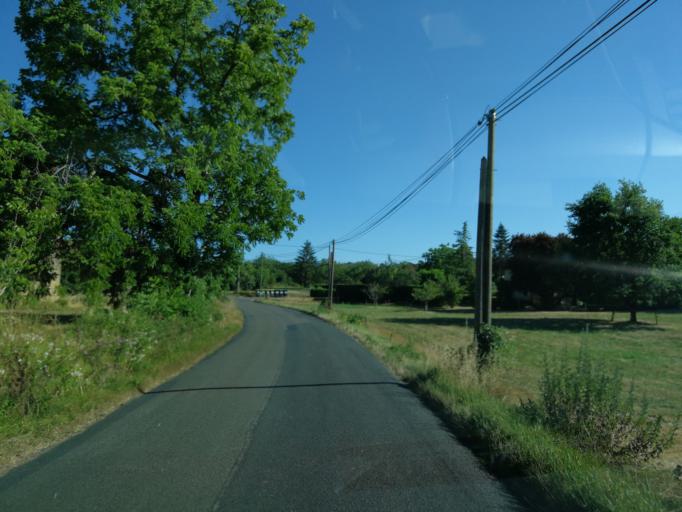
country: FR
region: Midi-Pyrenees
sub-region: Departement du Lot
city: Gourdon
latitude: 44.7777
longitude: 1.3652
